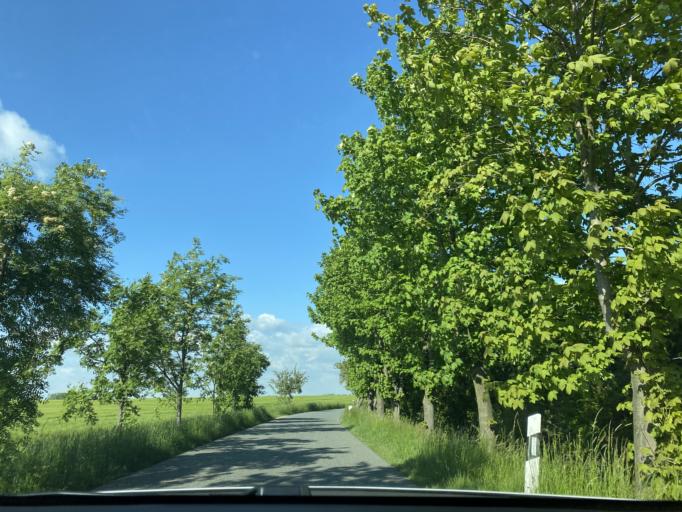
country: DE
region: Saxony
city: Reichenbach
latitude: 51.1186
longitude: 14.8376
